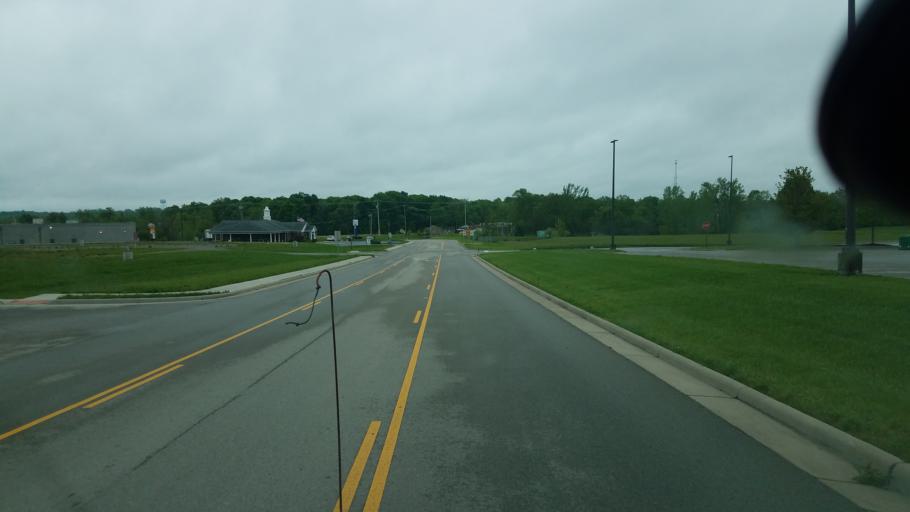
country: US
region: Ohio
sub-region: Highland County
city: Hillsboro
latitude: 39.2275
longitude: -83.6252
